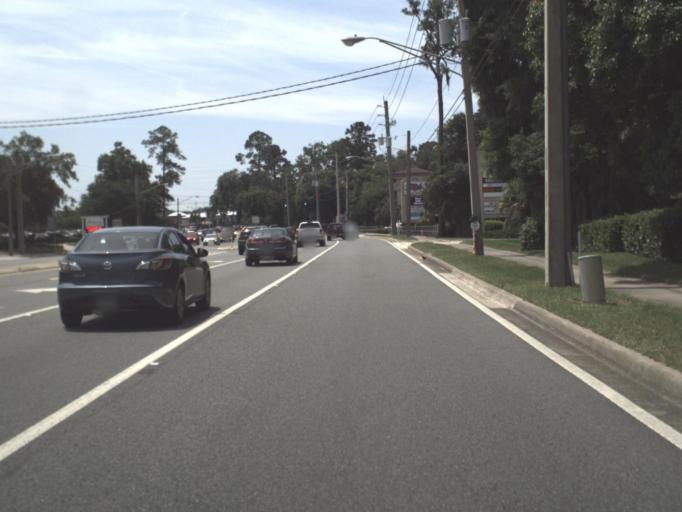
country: US
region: Florida
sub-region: Saint Johns County
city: Fruit Cove
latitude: 30.1378
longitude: -81.6327
